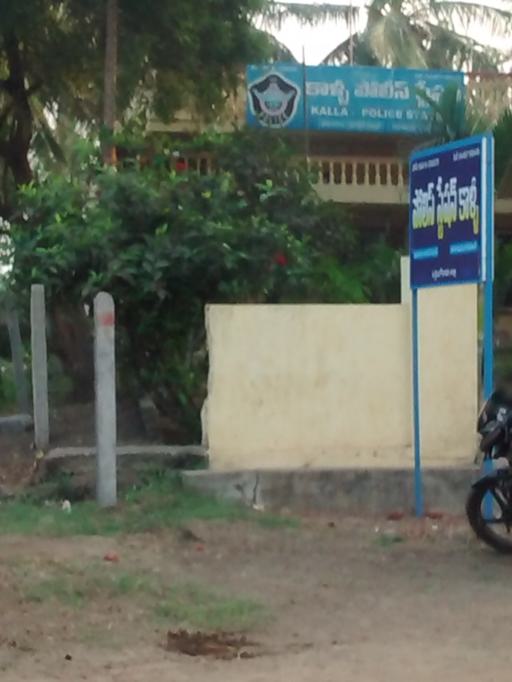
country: IN
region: Andhra Pradesh
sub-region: West Godavari
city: Akividu
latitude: 16.5351
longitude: 81.4003
